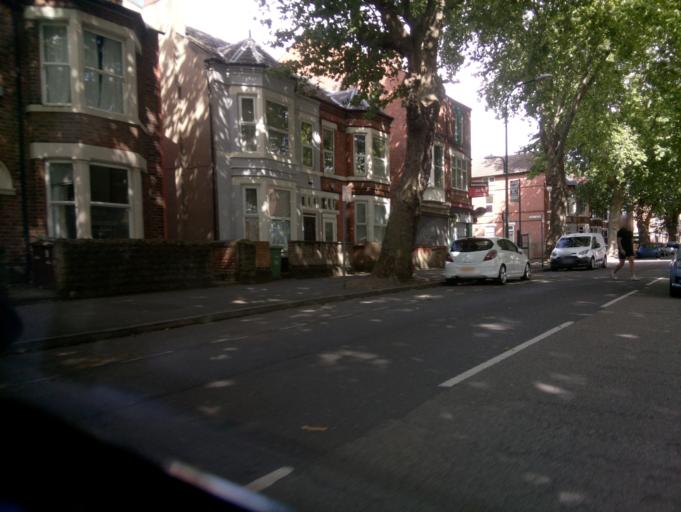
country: GB
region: England
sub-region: Nottingham
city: Nottingham
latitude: 52.9476
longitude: -1.1740
